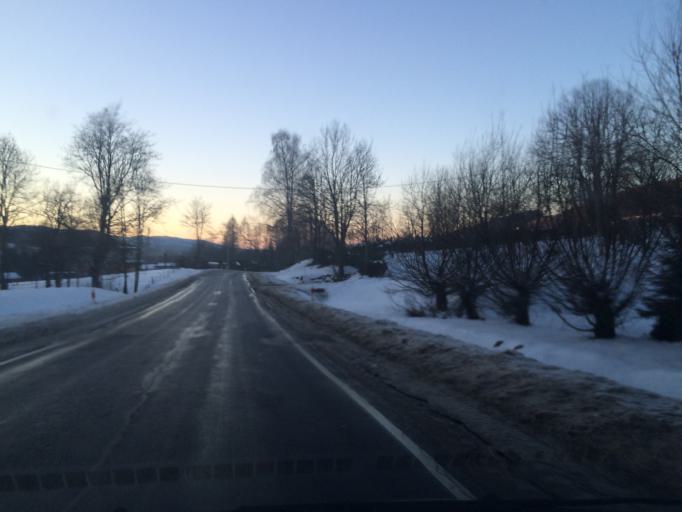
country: PL
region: Subcarpathian Voivodeship
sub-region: Powiat bieszczadzki
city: Czarna
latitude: 49.3574
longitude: 22.6759
